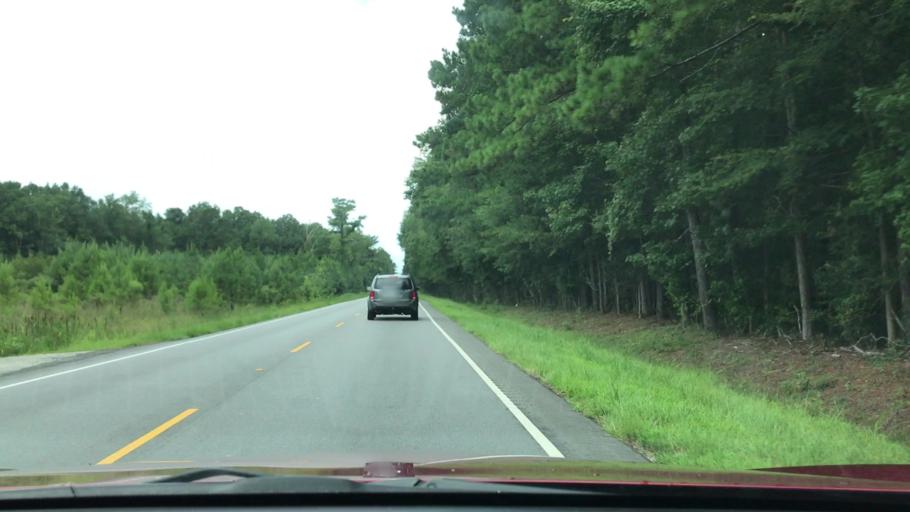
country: US
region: South Carolina
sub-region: Horry County
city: Loris
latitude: 33.9113
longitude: -78.8207
